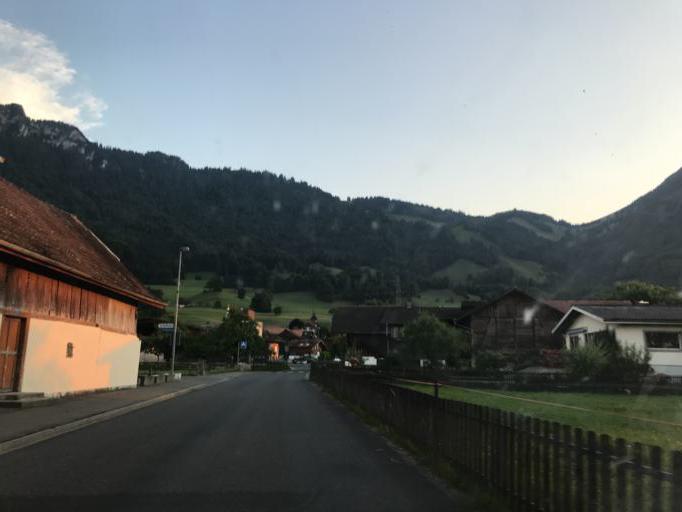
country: CH
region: Bern
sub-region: Frutigen-Niedersimmental District
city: Wimmis
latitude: 46.6960
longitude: 7.6234
